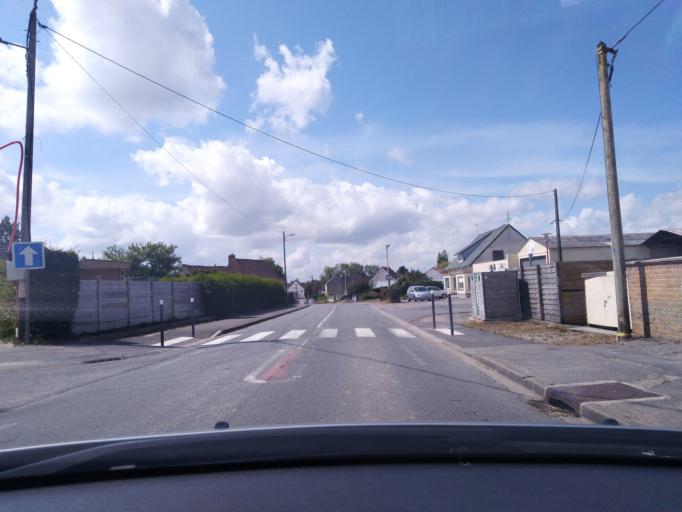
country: FR
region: Nord-Pas-de-Calais
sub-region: Departement du Pas-de-Calais
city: Ferques
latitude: 50.8342
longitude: 1.7601
